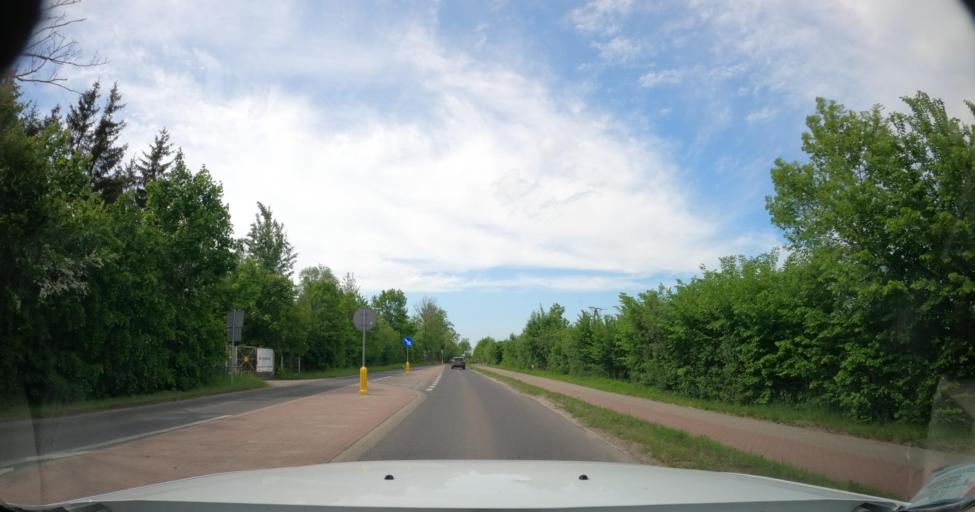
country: PL
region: Warmian-Masurian Voivodeship
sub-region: Powiat lidzbarski
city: Lidzbark Warminski
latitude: 54.1409
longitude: 20.5672
